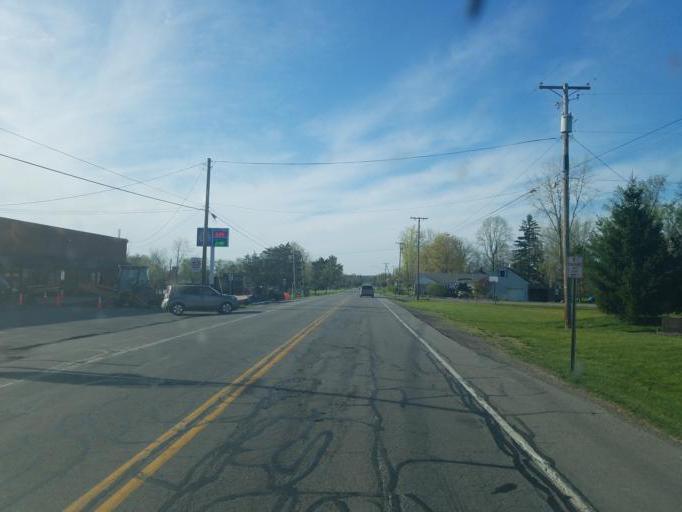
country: US
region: Ohio
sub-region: Ashland County
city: Ashland
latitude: 40.9444
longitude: -82.3585
